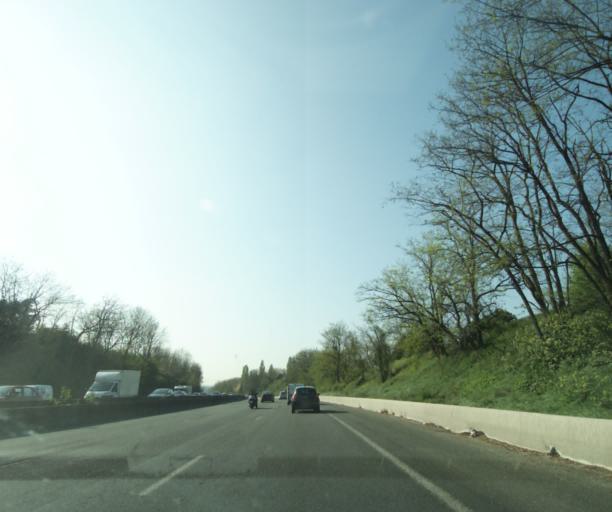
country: FR
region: Ile-de-France
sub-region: Departement de l'Essonne
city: Morsang-sur-Orge
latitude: 48.6662
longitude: 2.3619
